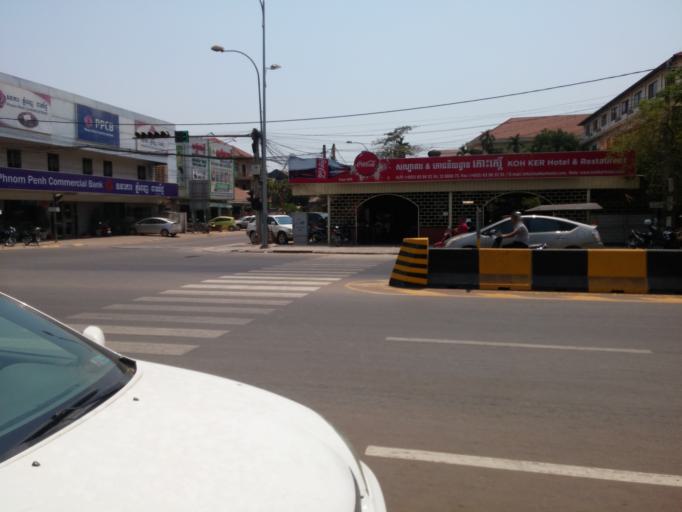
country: KH
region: Siem Reap
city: Siem Reap
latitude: 13.3611
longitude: 103.8616
